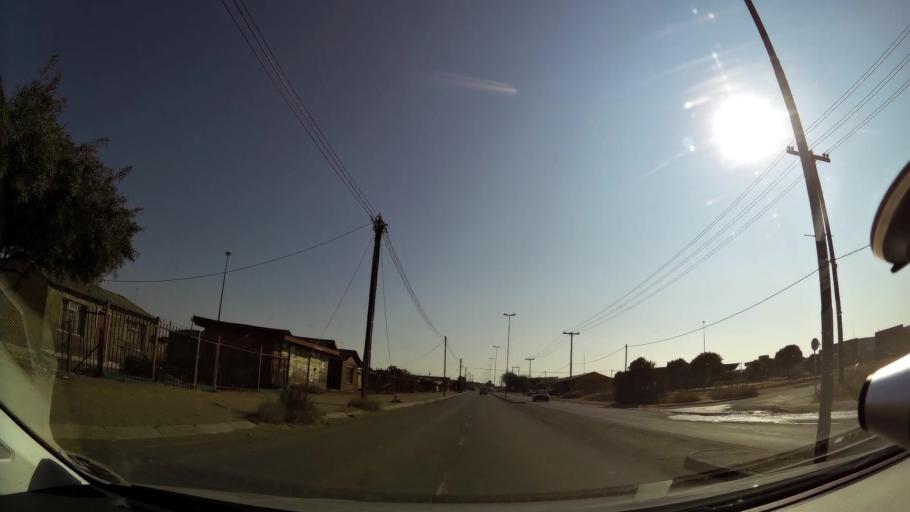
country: ZA
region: Orange Free State
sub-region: Mangaung Metropolitan Municipality
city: Bloemfontein
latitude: -29.1866
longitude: 26.2346
